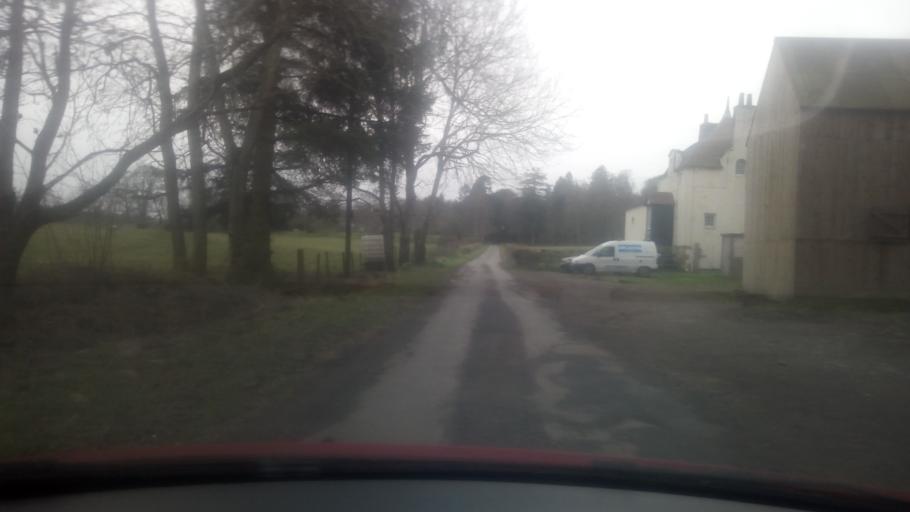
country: GB
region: Scotland
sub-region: The Scottish Borders
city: Jedburgh
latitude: 55.4487
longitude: -2.6399
